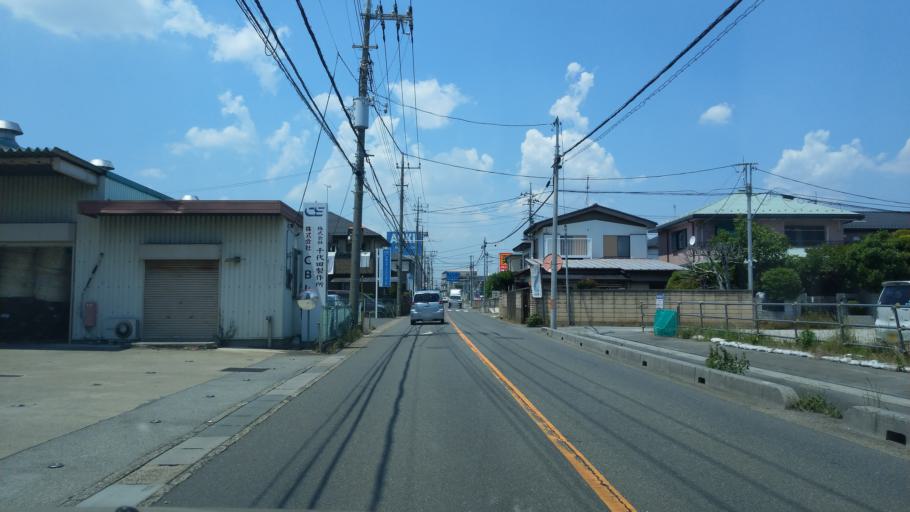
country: JP
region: Saitama
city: Saitama
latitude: 35.8703
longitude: 139.6791
